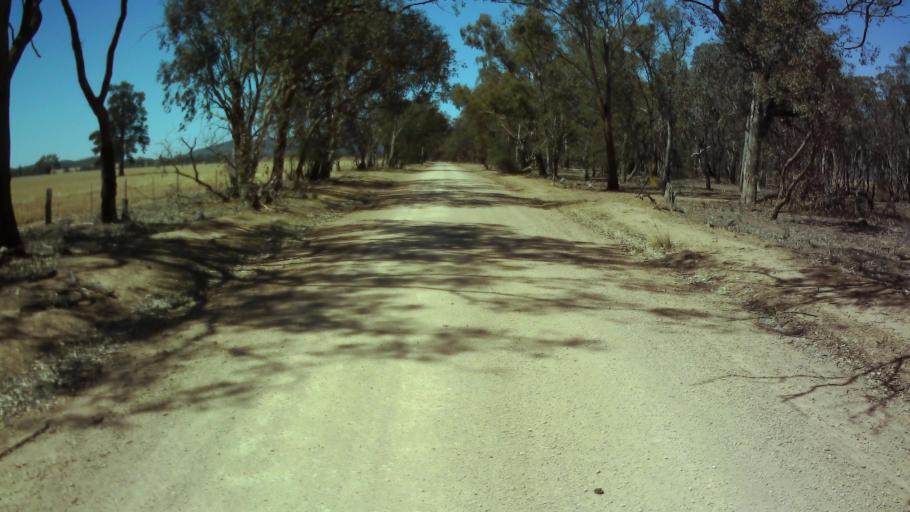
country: AU
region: New South Wales
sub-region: Weddin
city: Grenfell
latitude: -33.9170
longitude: 148.0792
